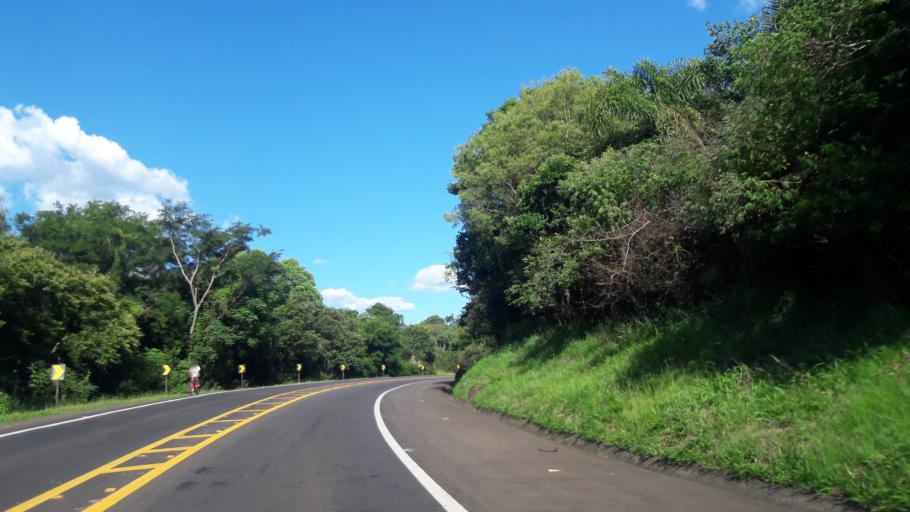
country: BR
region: Parana
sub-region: Laranjeiras Do Sul
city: Laranjeiras do Sul
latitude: -25.4194
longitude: -52.0349
